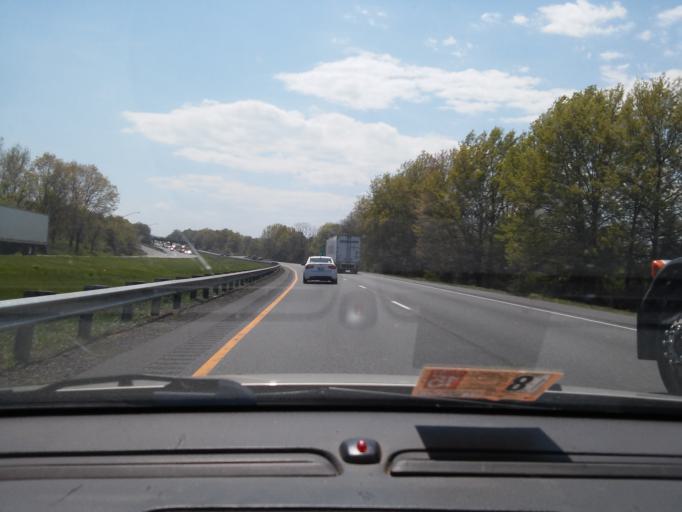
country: US
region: Maryland
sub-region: Washington County
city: Williamsport
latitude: 39.6117
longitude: -77.7994
